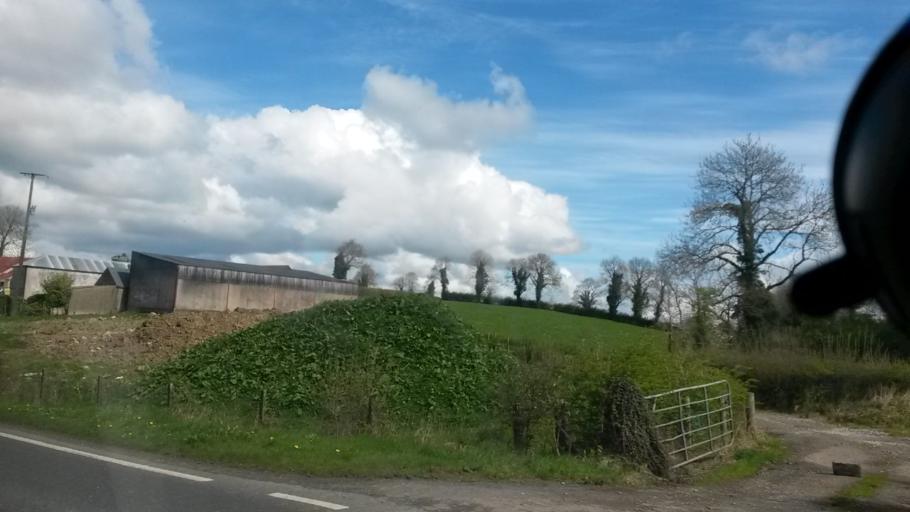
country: IE
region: Ulster
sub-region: An Cabhan
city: Ballyconnell
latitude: 54.1458
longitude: -7.5164
